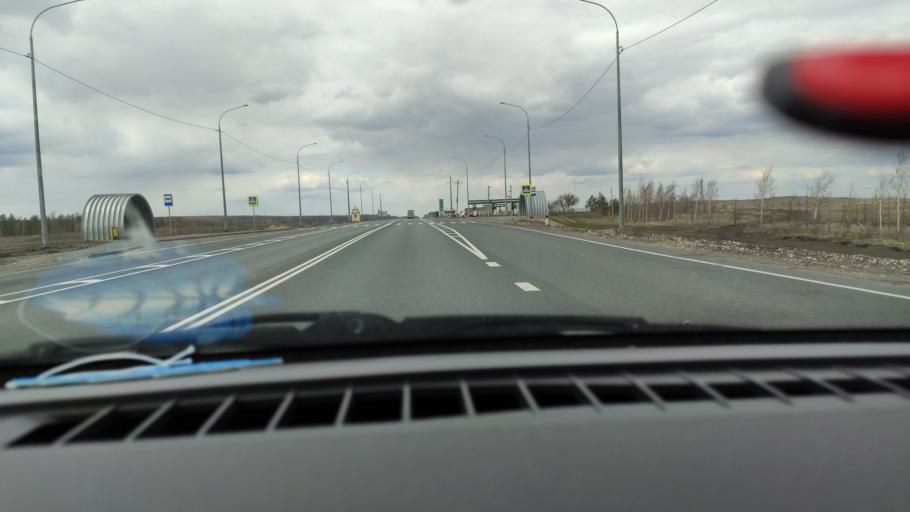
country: RU
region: Saratov
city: Shikhany
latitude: 52.1337
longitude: 47.2237
